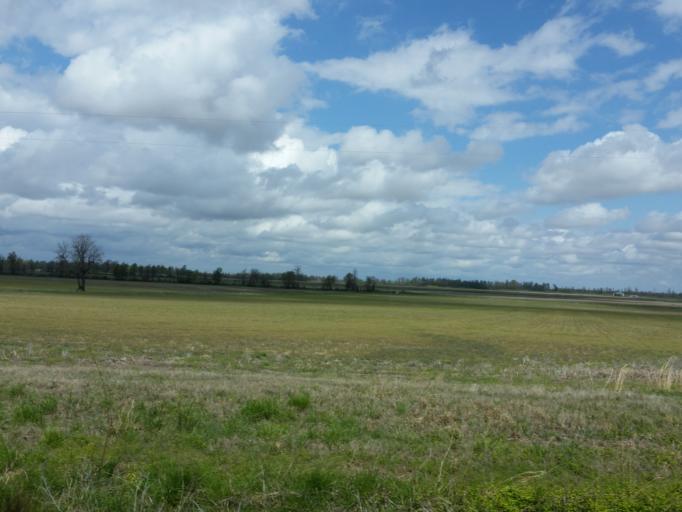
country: US
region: Arkansas
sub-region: Greene County
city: Paragould
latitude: 36.2185
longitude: -90.5618
